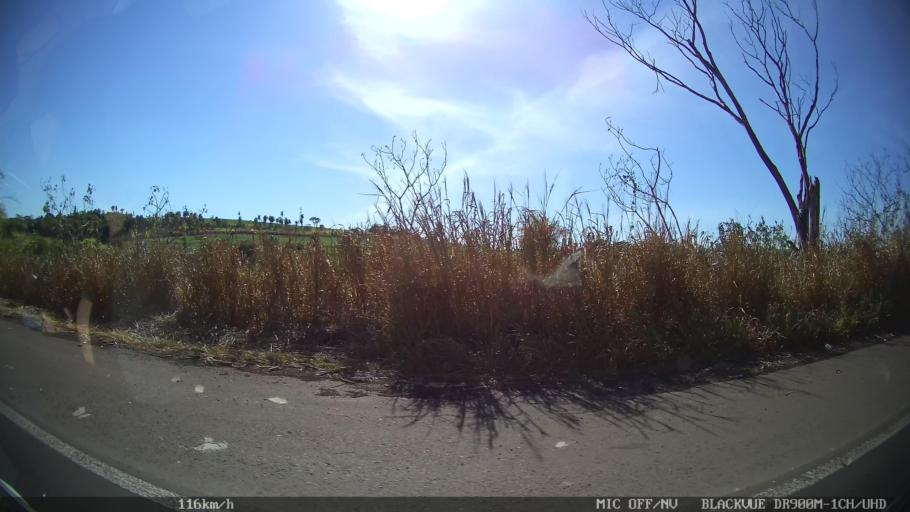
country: BR
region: Sao Paulo
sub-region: Olimpia
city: Olimpia
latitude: -20.6313
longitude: -48.8110
